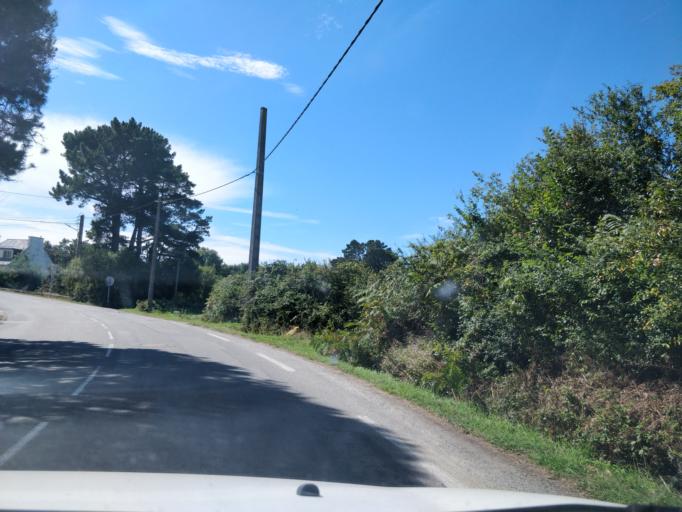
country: FR
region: Brittany
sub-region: Departement du Morbihan
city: Saint-Philibert
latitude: 47.5837
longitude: -2.9999
